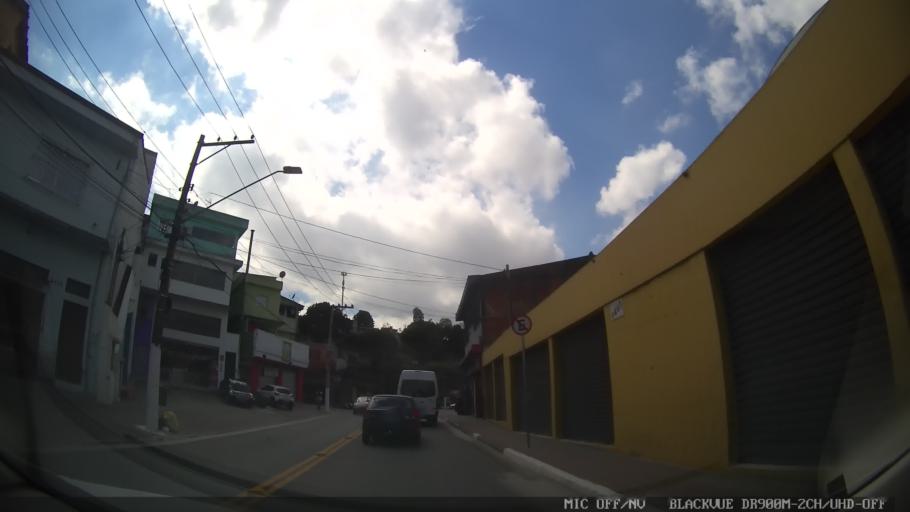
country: BR
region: Sao Paulo
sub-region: Caieiras
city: Caieiras
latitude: -23.4045
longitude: -46.7490
